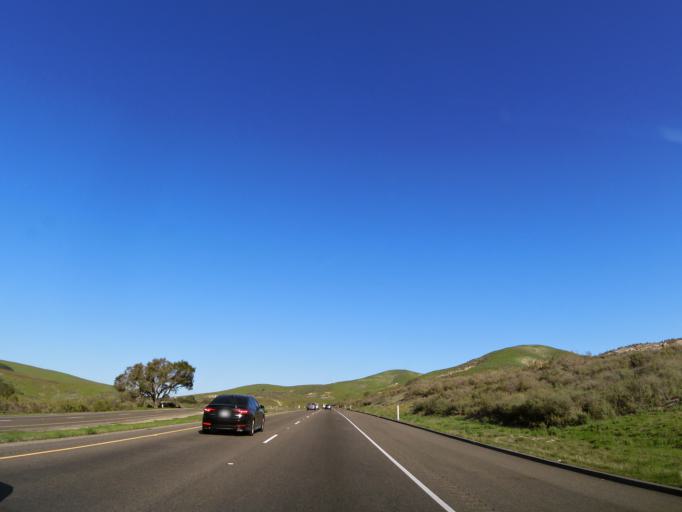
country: US
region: California
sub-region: Santa Barbara County
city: Los Alamos
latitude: 34.8115
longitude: -120.3458
